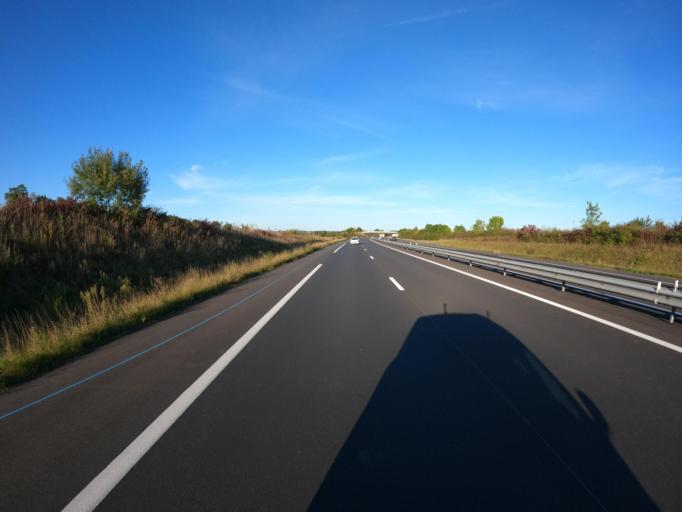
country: FR
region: Pays de la Loire
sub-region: Departement de la Vendee
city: Beaurepaire
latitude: 46.8908
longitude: -1.0965
